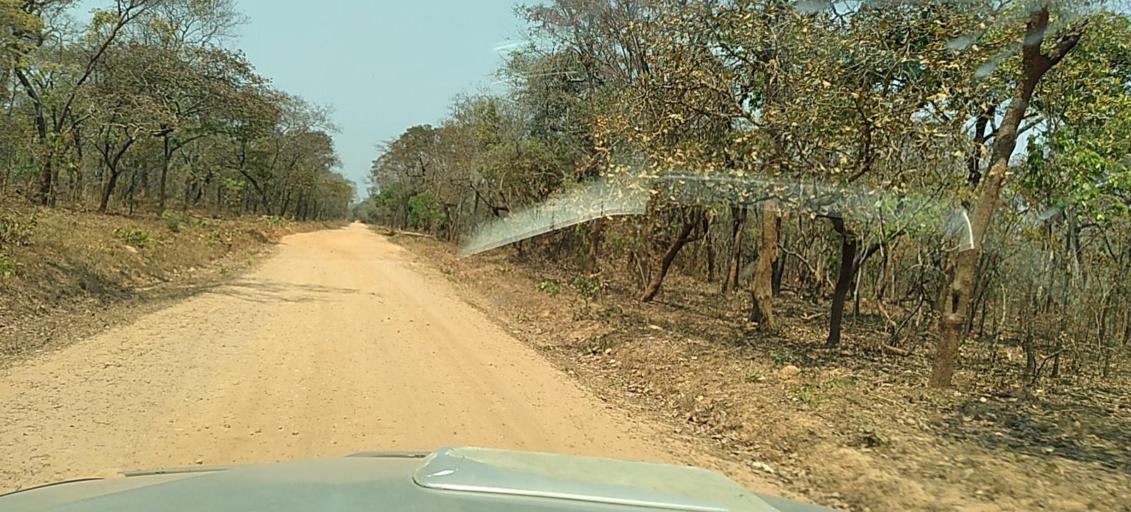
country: ZM
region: North-Western
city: Kasempa
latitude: -13.6615
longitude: 26.2720
